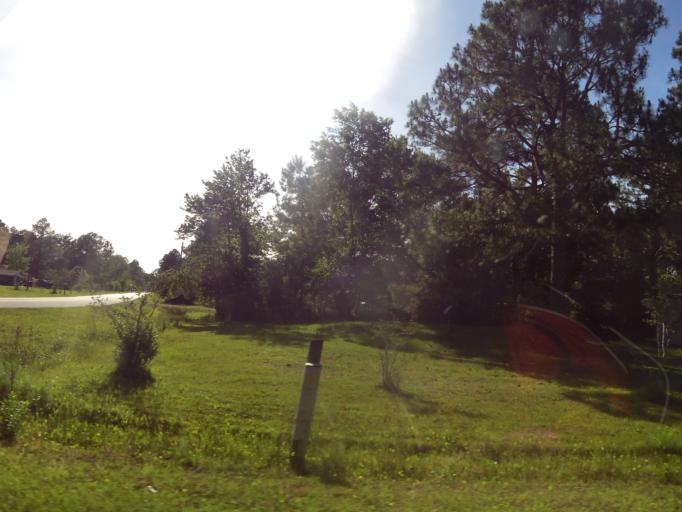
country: US
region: Florida
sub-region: Nassau County
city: Nassau Village-Ratliff
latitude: 30.5231
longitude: -81.7780
